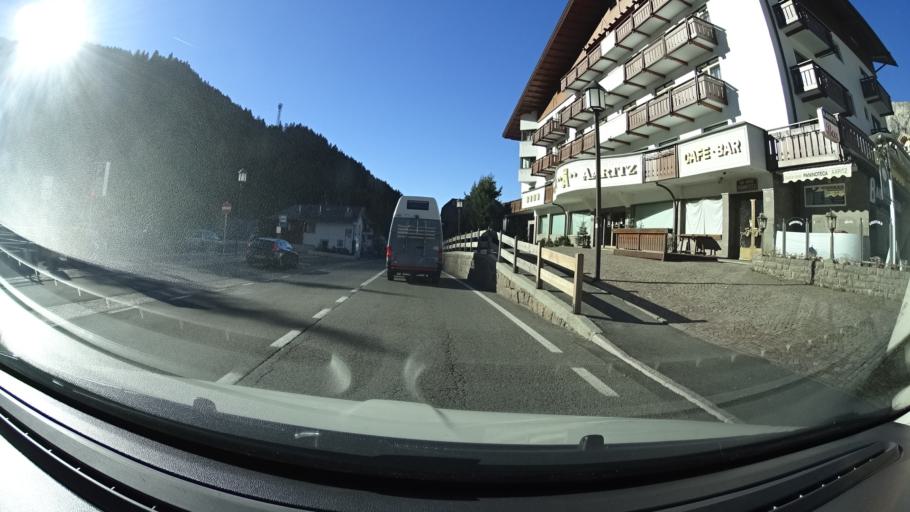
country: IT
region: Trentino-Alto Adige
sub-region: Bolzano
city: Selva
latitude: 46.5534
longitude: 11.7618
